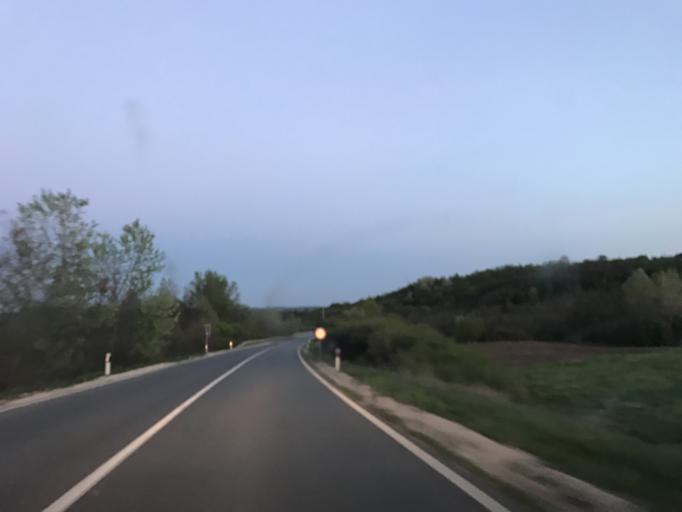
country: RS
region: Central Serbia
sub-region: Zajecarski Okrug
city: Zajecar
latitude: 43.9497
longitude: 22.3023
